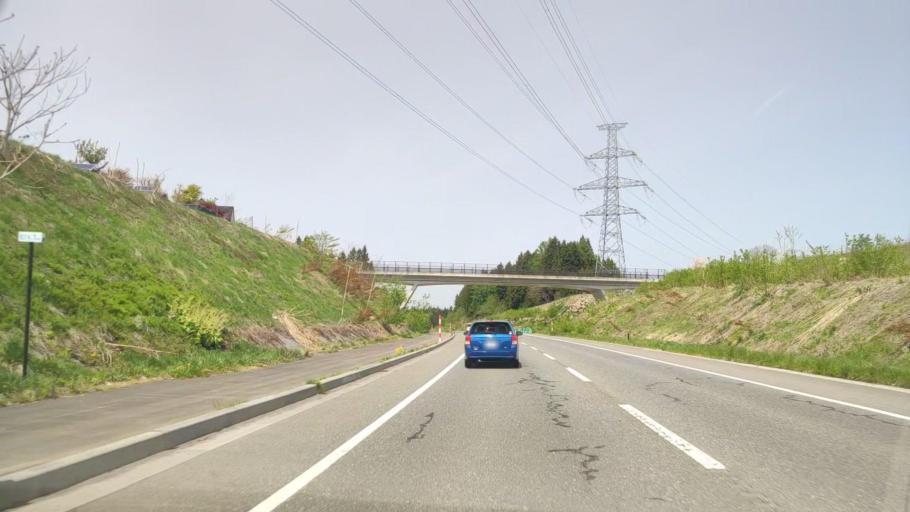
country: JP
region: Aomori
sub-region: Misawa Shi
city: Inuotose
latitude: 40.6843
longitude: 141.1704
